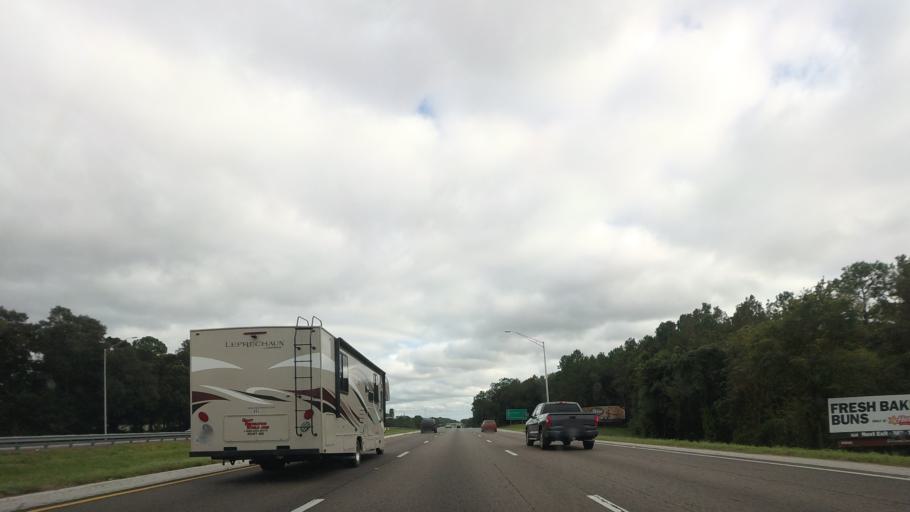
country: US
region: Florida
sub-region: Alachua County
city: Alachua
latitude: 29.6818
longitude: -82.4399
